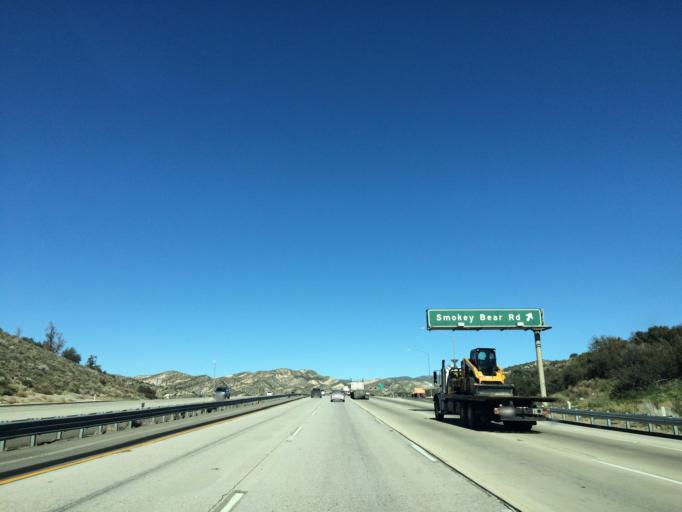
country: US
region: California
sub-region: Kern County
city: Lebec
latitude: 34.7042
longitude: -118.7944
